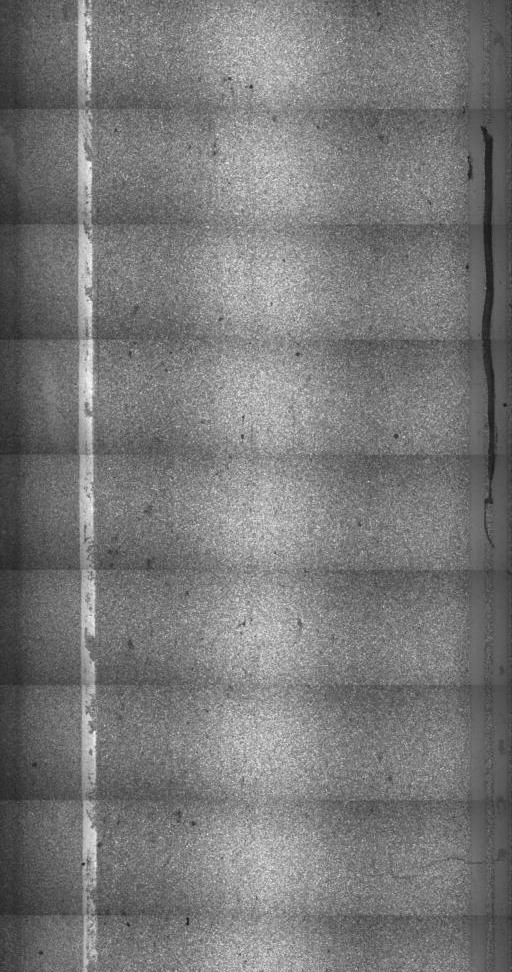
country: US
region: Vermont
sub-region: Franklin County
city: Swanton
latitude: 44.8919
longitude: -73.0911
